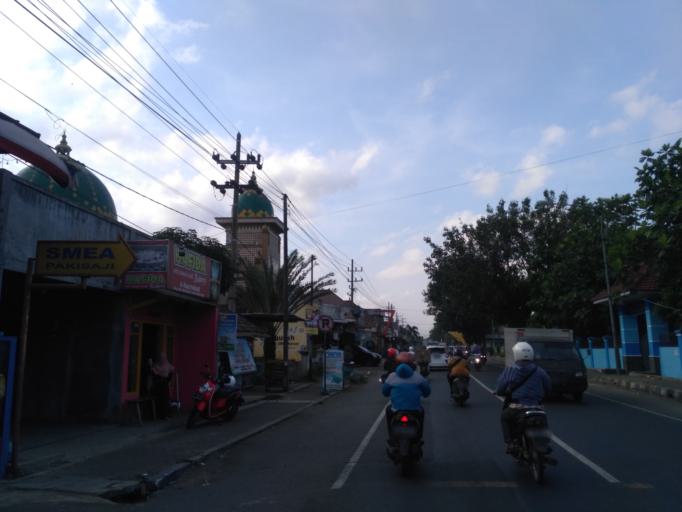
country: ID
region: East Java
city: Pakisaji
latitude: -8.0656
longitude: 112.5989
